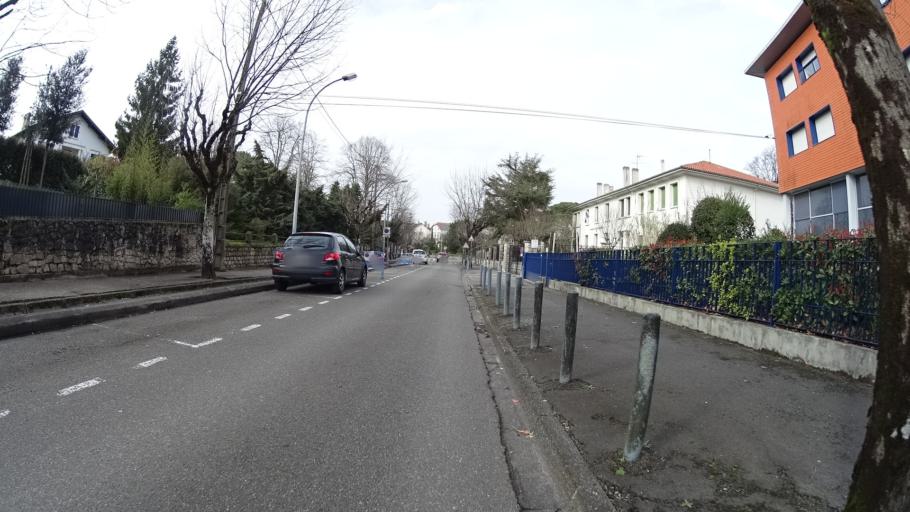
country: FR
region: Aquitaine
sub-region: Departement des Landes
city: Dax
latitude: 43.7029
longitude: -1.0566
